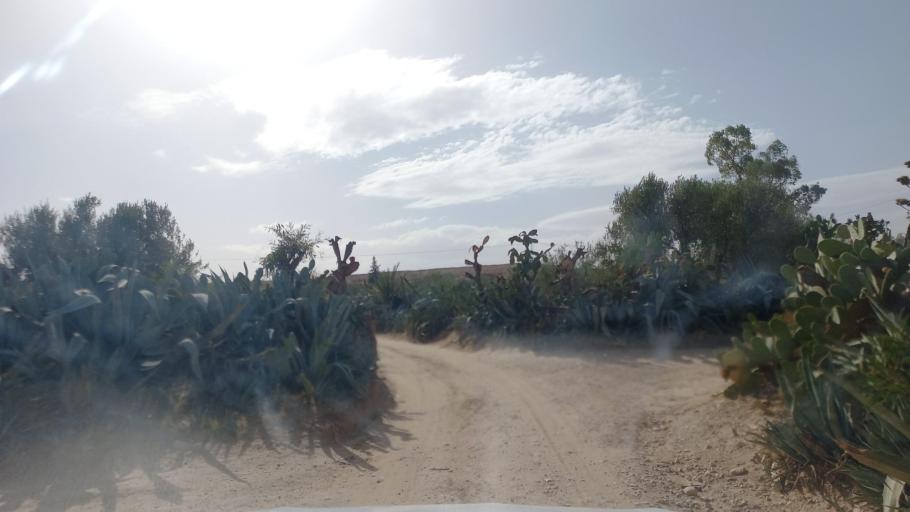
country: TN
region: Al Qasrayn
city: Kasserine
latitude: 35.2622
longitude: 8.9286
